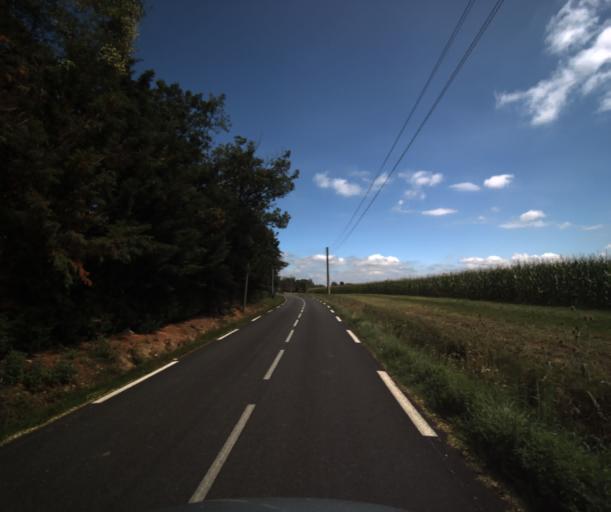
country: FR
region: Midi-Pyrenees
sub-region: Departement de la Haute-Garonne
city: Lacasse
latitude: 43.3864
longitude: 1.2490
